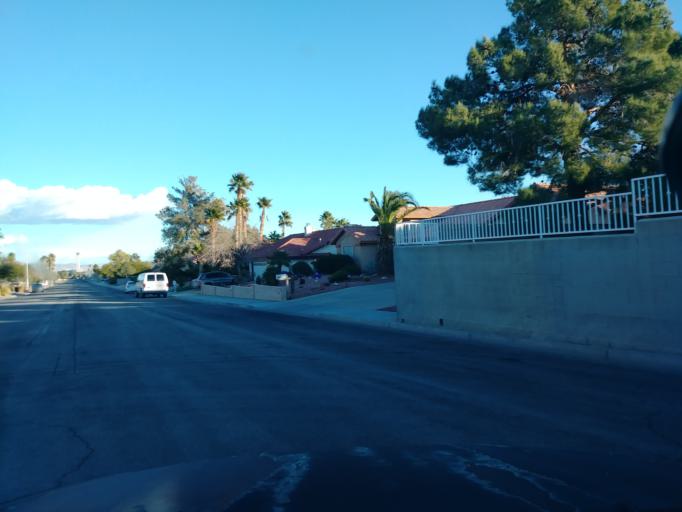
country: US
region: Nevada
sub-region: Clark County
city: Spring Valley
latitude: 36.1479
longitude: -115.2421
